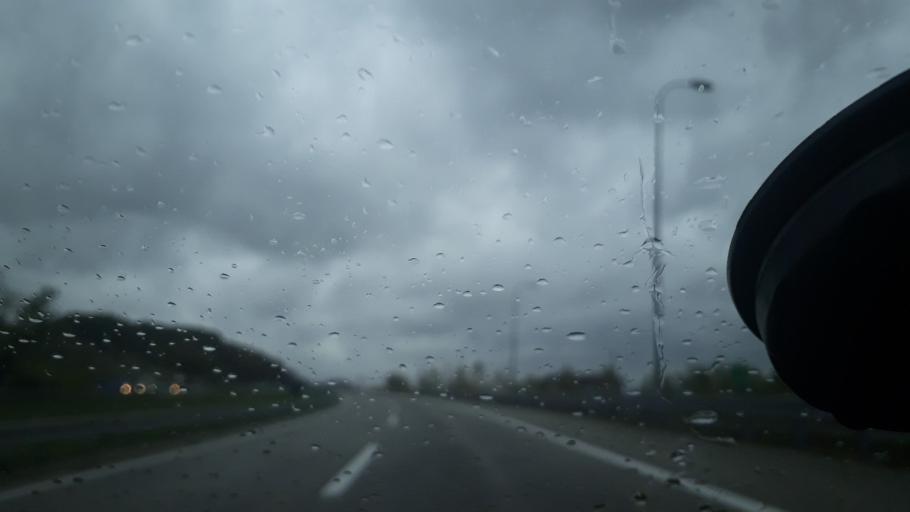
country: BA
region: Republika Srpska
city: Laktasi
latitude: 44.8738
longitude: 17.2808
